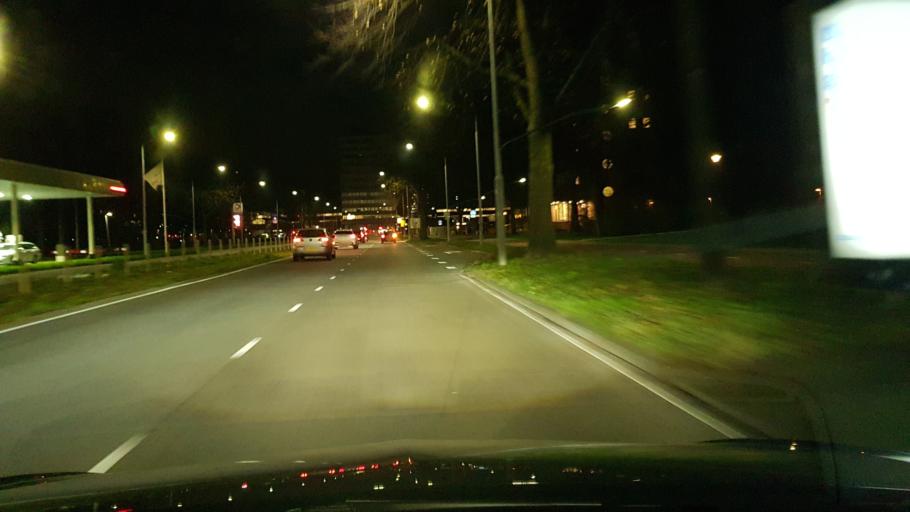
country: NL
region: North Holland
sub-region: Gemeente Haarlem
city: Haarlem
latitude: 52.3634
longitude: 4.6542
